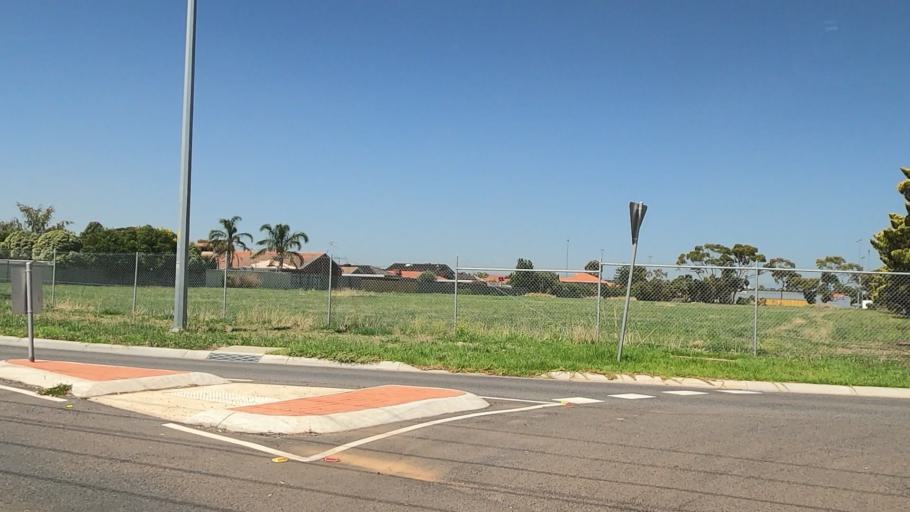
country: AU
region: Victoria
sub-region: Hume
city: Attwood
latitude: -37.6490
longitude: 144.8894
